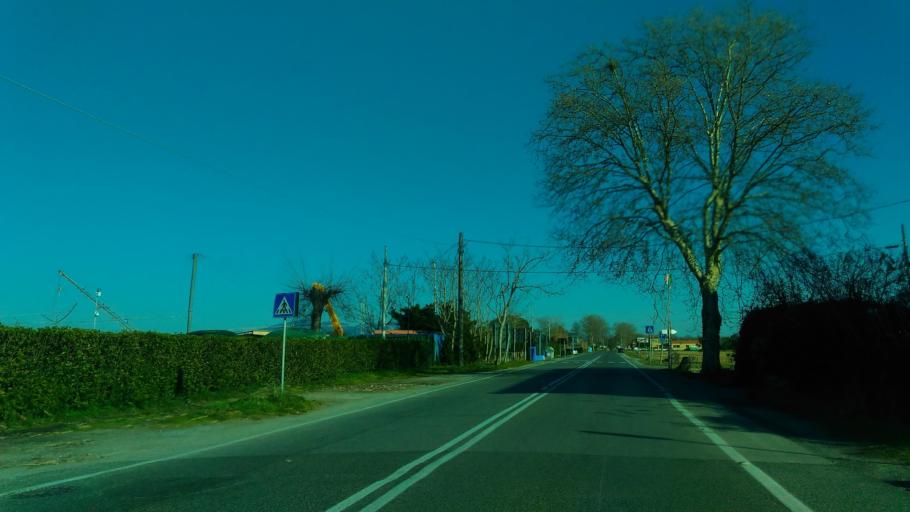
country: IT
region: Tuscany
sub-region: Province of Pisa
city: Marina di Pisa
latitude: 43.6791
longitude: 10.2780
